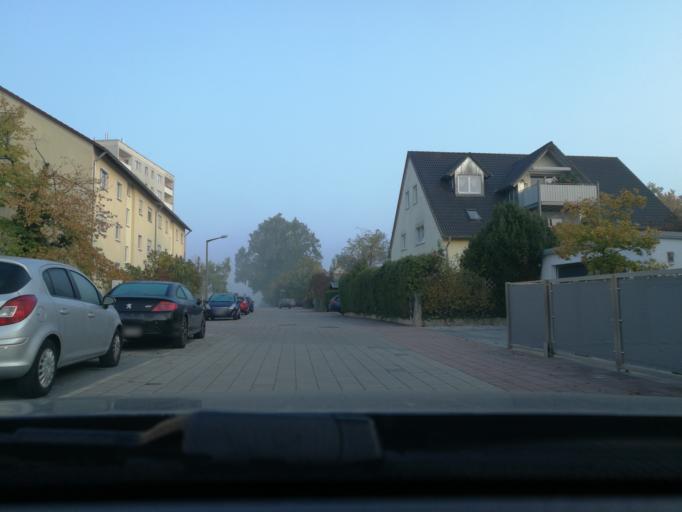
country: DE
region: Bavaria
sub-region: Regierungsbezirk Mittelfranken
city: Furth
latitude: 49.4883
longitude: 10.9566
